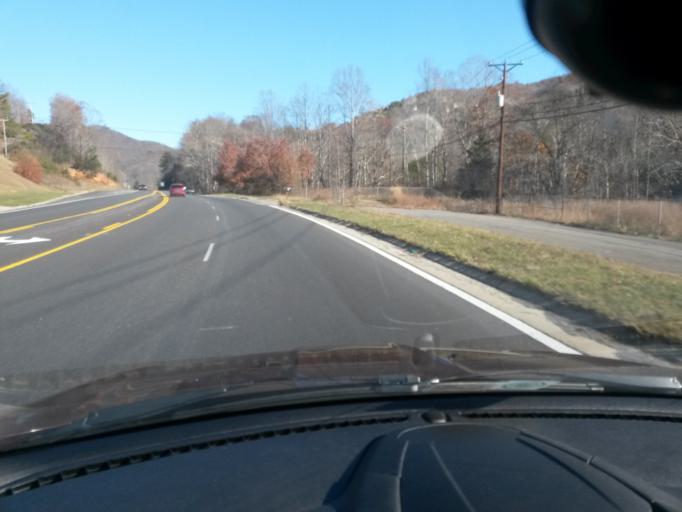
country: US
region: Virginia
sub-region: Patrick County
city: Stuart
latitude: 36.6598
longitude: -80.2764
